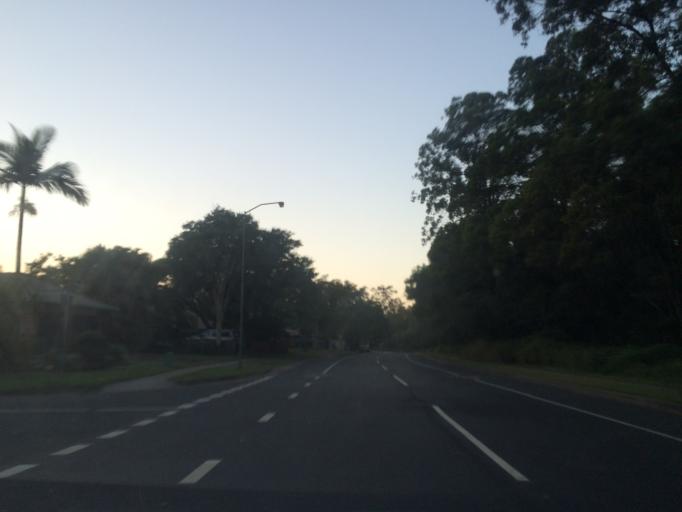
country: AU
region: Queensland
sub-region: Brisbane
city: Kenmore Hills
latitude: -27.4887
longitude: 152.9399
